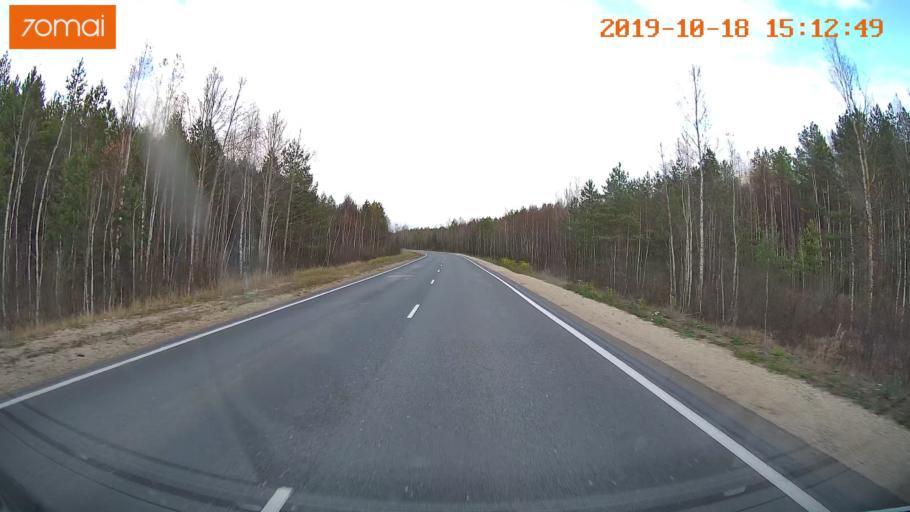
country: RU
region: Vladimir
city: Gus'-Khrustal'nyy
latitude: 55.5790
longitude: 40.7068
